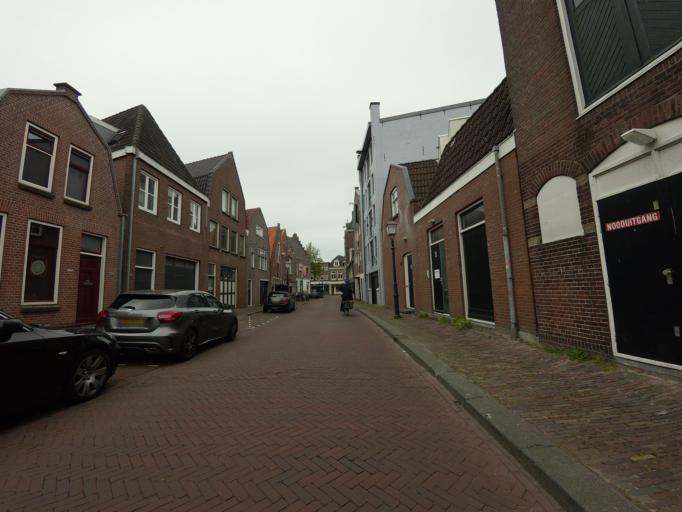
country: NL
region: North Holland
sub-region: Gemeente Hoorn
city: Hoorn
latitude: 52.6418
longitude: 5.0547
